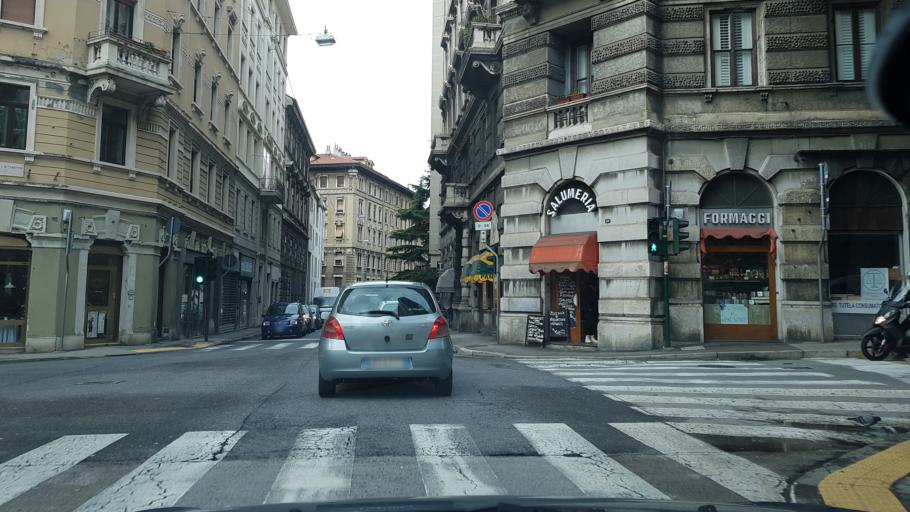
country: IT
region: Friuli Venezia Giulia
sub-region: Provincia di Trieste
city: Trieste
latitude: 45.6562
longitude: 13.7751
